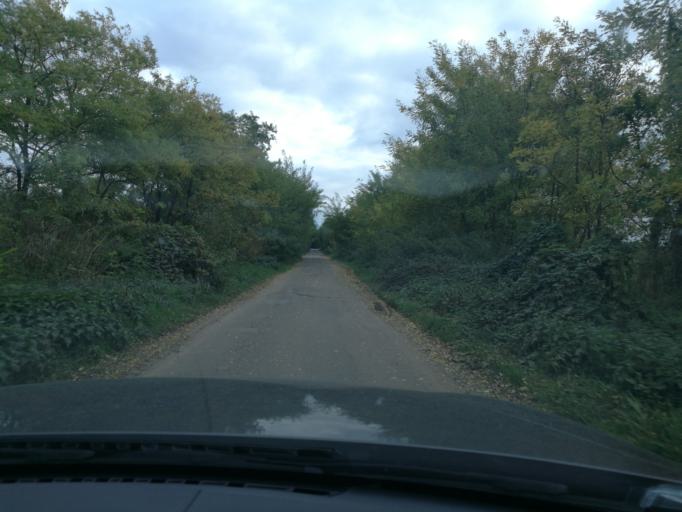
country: HU
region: Szabolcs-Szatmar-Bereg
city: Apagy
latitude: 47.9947
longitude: 21.8854
